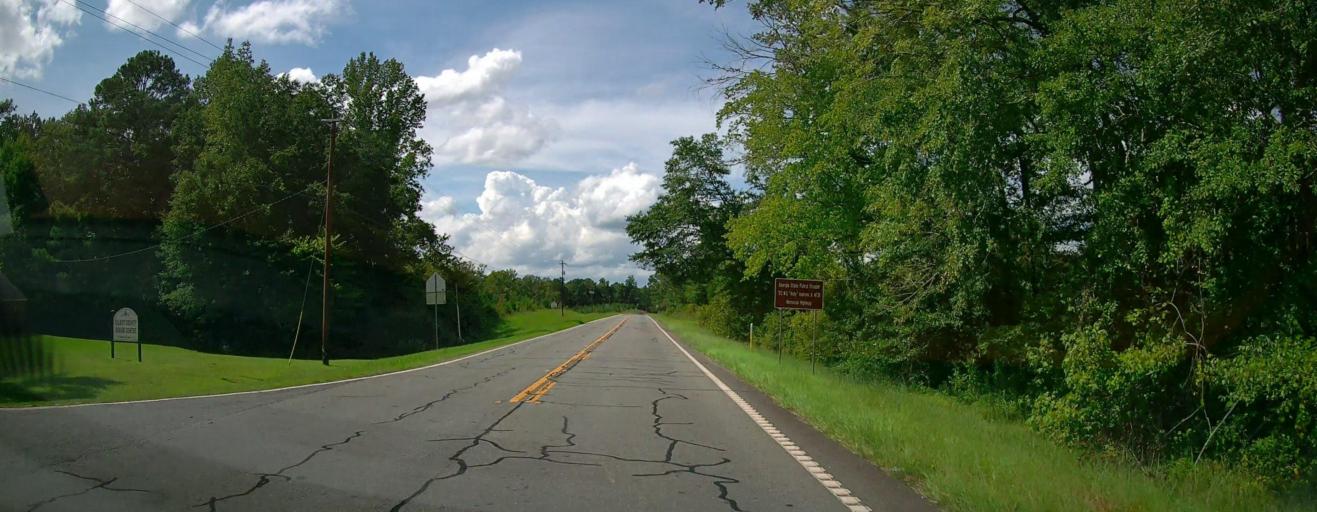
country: US
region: Georgia
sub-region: Talbot County
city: Talbotton
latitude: 32.6925
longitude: -84.5446
